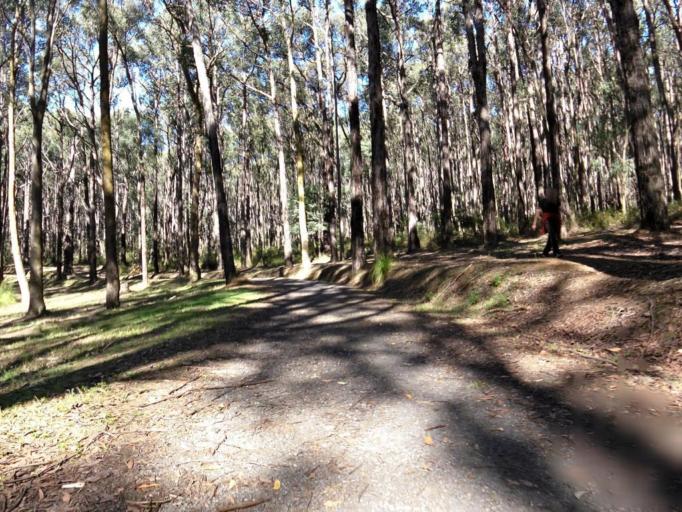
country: AU
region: Victoria
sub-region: Cardinia
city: Cockatoo
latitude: -37.9303
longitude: 145.4718
